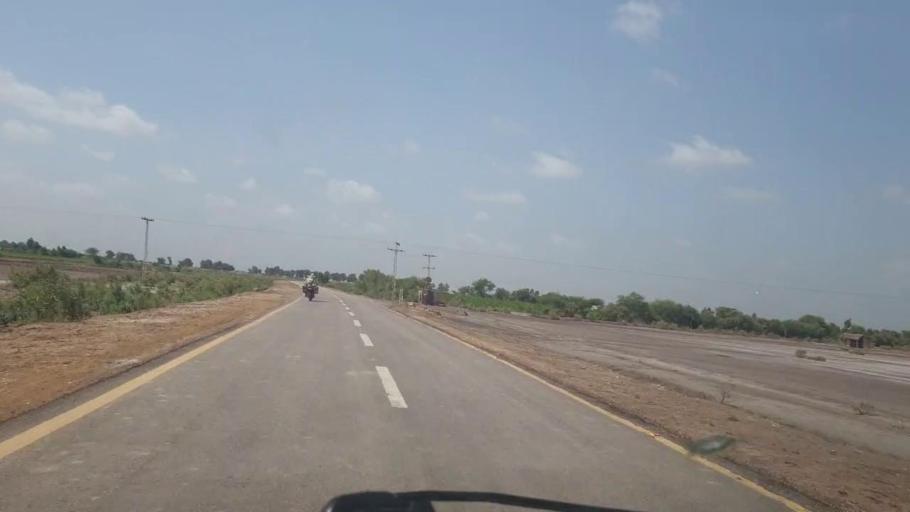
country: PK
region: Sindh
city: Berani
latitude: 25.7099
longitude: 68.9427
